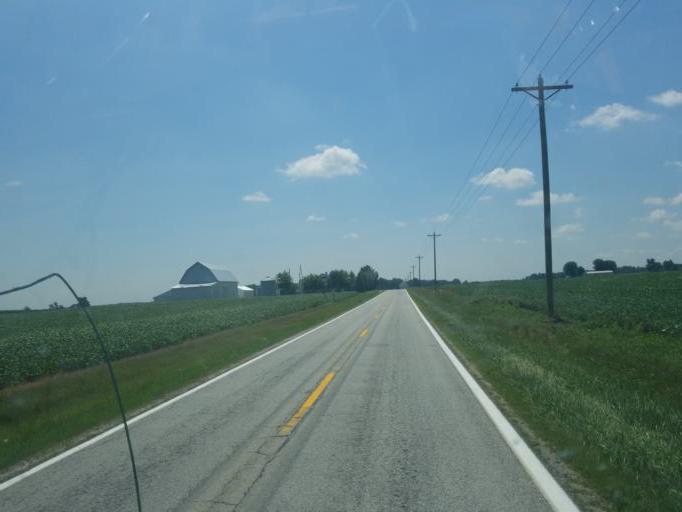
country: US
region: Ohio
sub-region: Allen County
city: Spencerville
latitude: 40.6825
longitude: -84.4255
